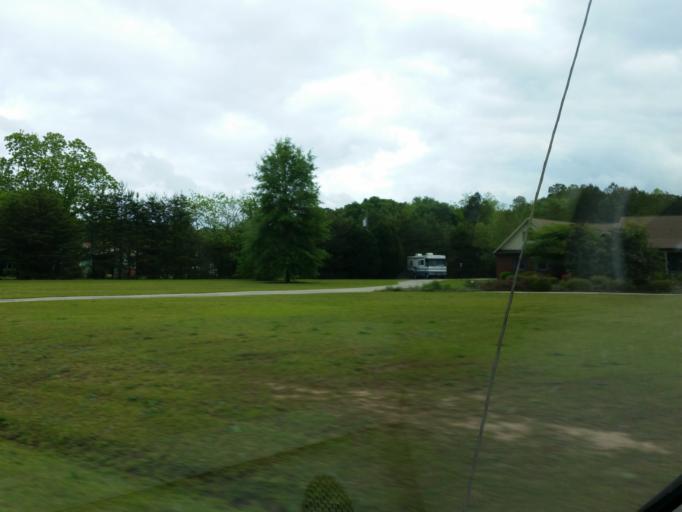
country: US
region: Georgia
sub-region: Peach County
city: Byron
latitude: 32.6517
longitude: -83.7991
